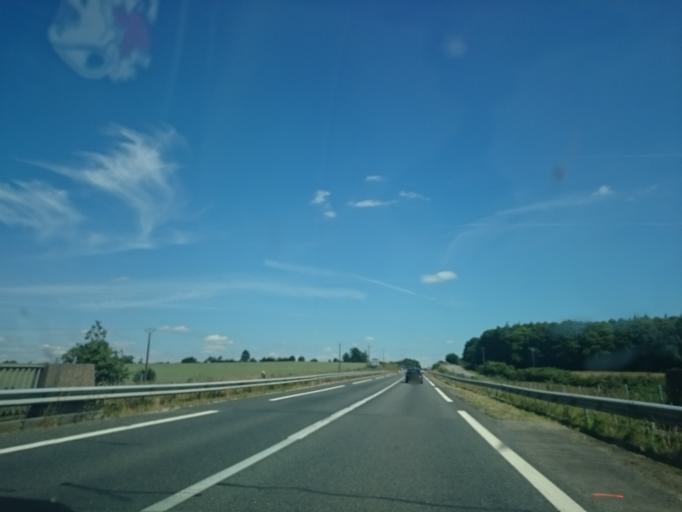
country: FR
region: Brittany
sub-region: Departement des Cotes-d'Armor
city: Plouguernevel
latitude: 48.2396
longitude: -3.2247
